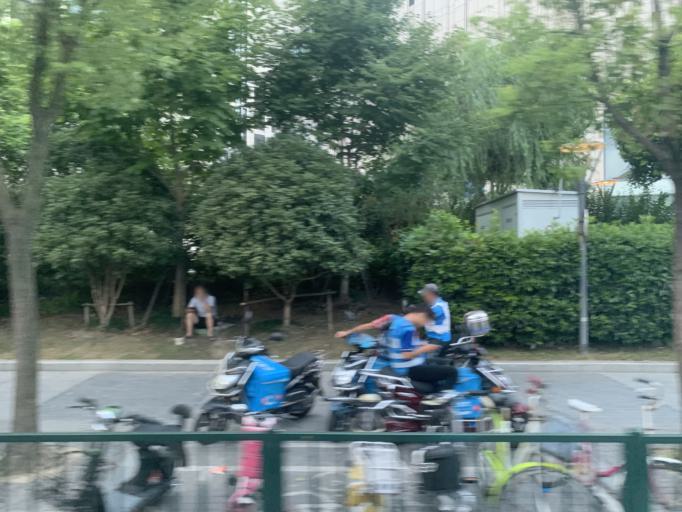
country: CN
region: Shanghai Shi
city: Pudong
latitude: 31.2323
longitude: 121.5242
